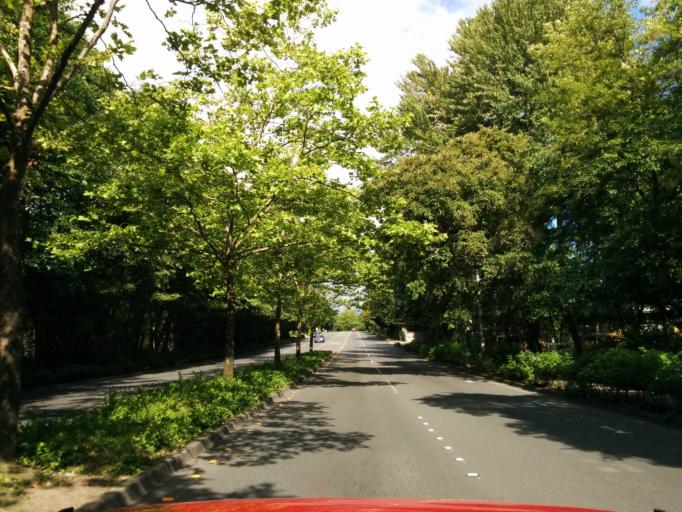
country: US
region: Washington
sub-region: King County
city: Eastgate
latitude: 47.6170
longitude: -122.1407
